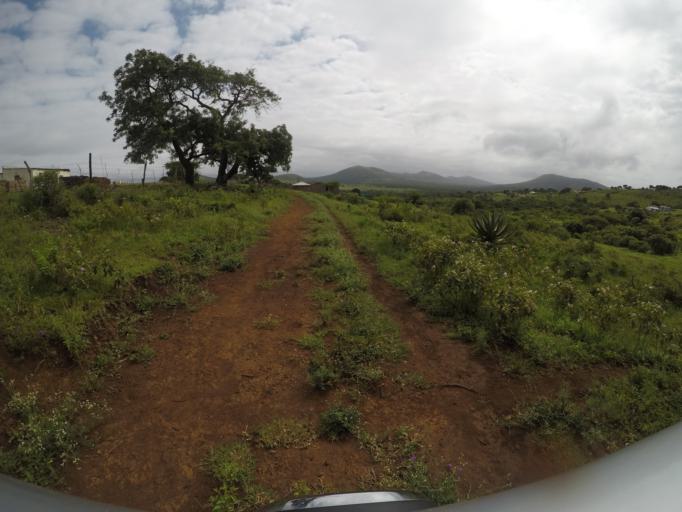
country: ZA
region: KwaZulu-Natal
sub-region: uThungulu District Municipality
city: Empangeni
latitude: -28.6279
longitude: 31.8638
